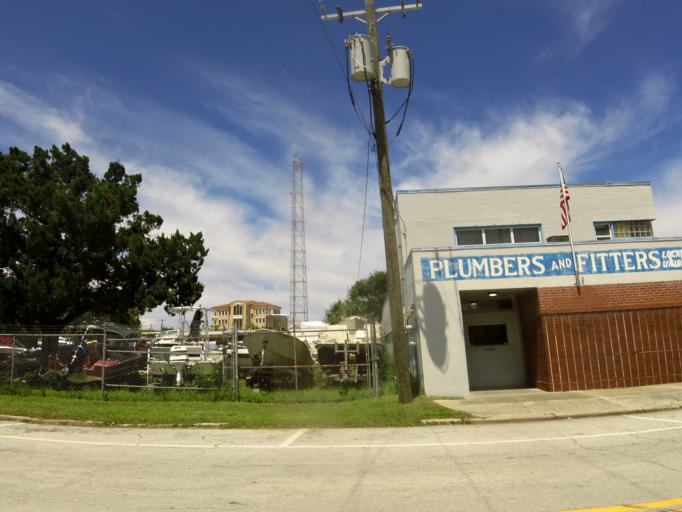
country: US
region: Florida
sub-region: Volusia County
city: Daytona Beach
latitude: 29.2268
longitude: -81.0259
